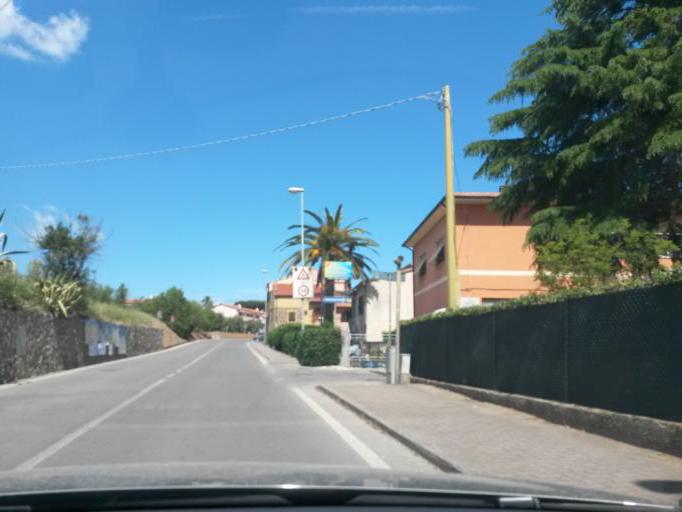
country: IT
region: Tuscany
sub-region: Provincia di Livorno
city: Porto Azzurro
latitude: 42.7691
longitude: 10.3961
